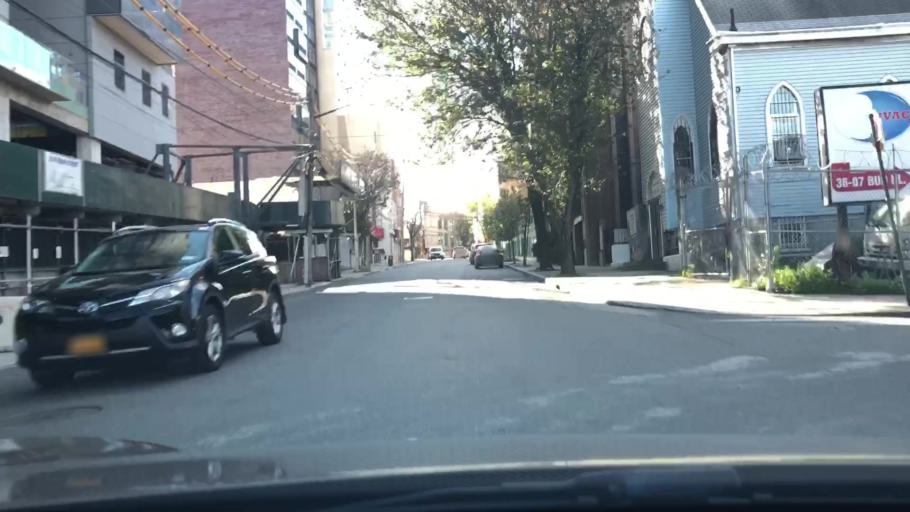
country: US
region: New York
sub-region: Queens County
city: Jamaica
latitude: 40.7624
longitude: -73.8332
